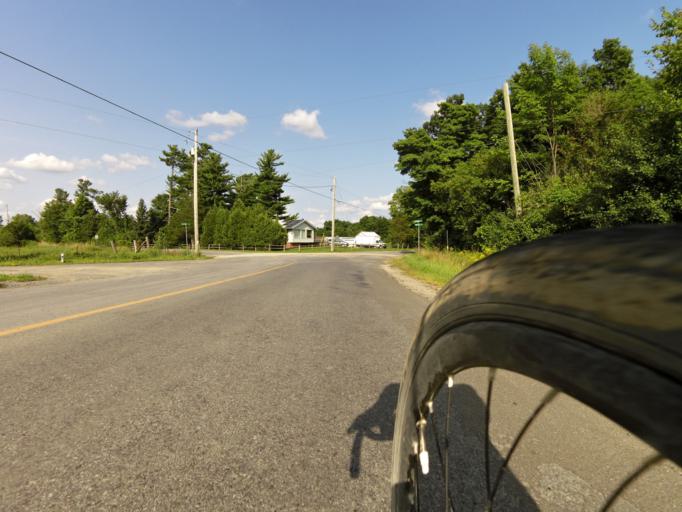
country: CA
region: Ontario
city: Kingston
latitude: 44.3683
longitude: -76.6186
